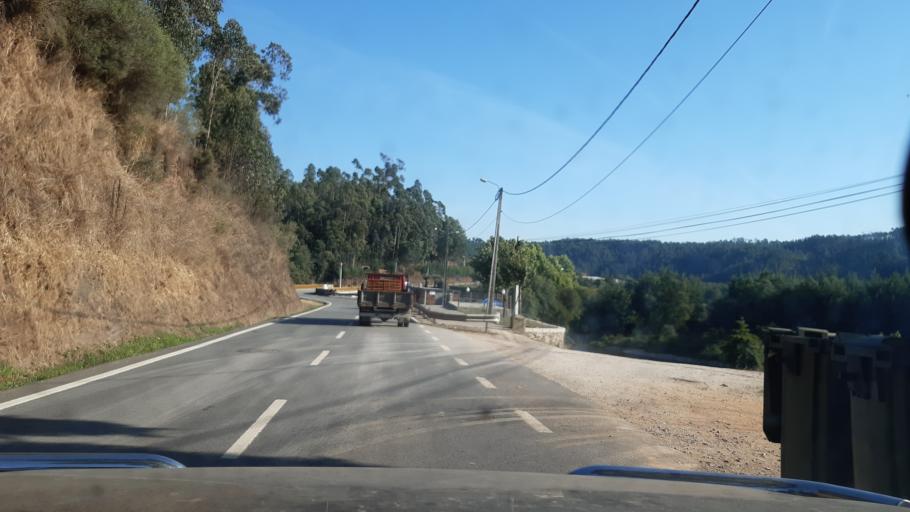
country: PT
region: Aveiro
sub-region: Agueda
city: Agueda
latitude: 40.5670
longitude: -8.4006
